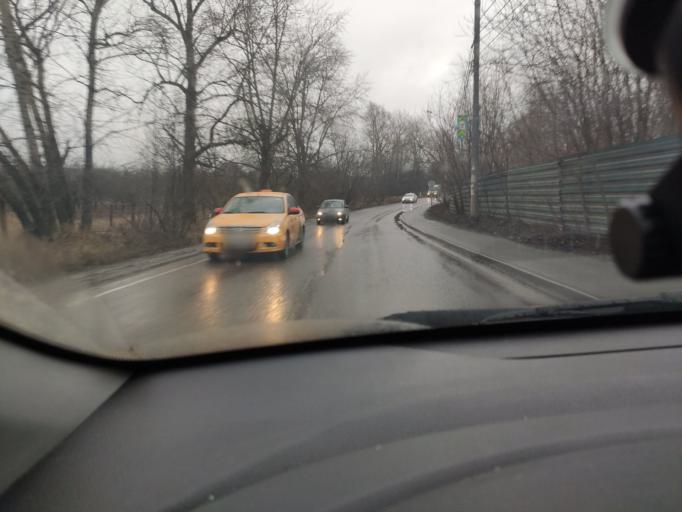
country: RU
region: Moscow
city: Zagor'ye
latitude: 55.5633
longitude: 37.6598
